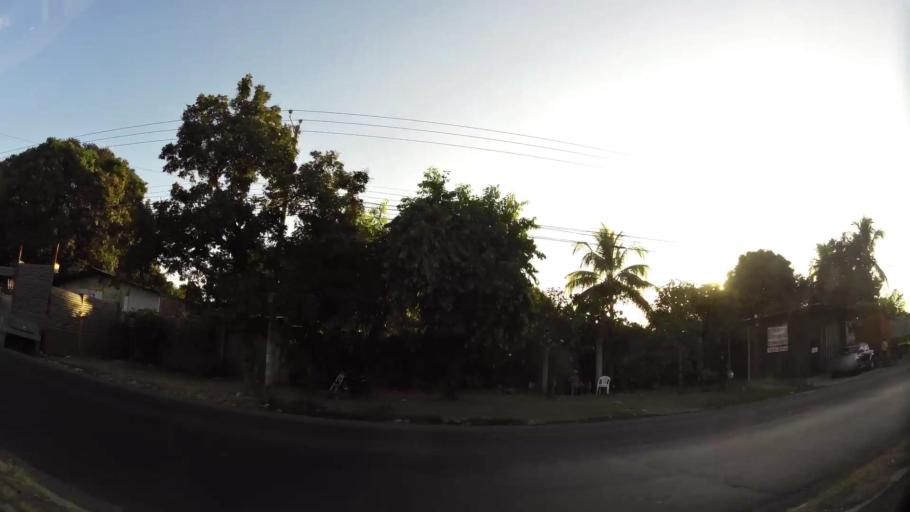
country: SV
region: La Libertad
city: Santa Tecla
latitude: 13.7271
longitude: -89.3770
